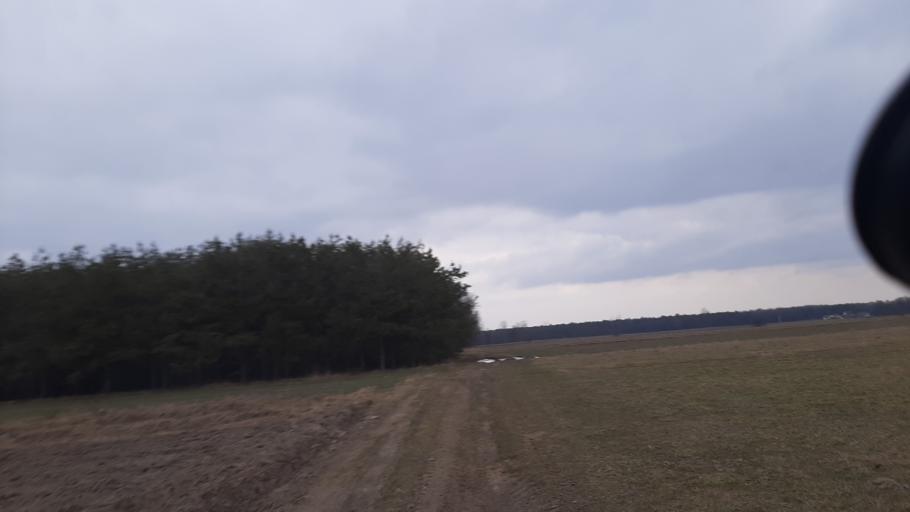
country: PL
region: Lublin Voivodeship
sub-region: Powiat lubelski
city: Garbow
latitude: 51.3844
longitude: 22.4073
